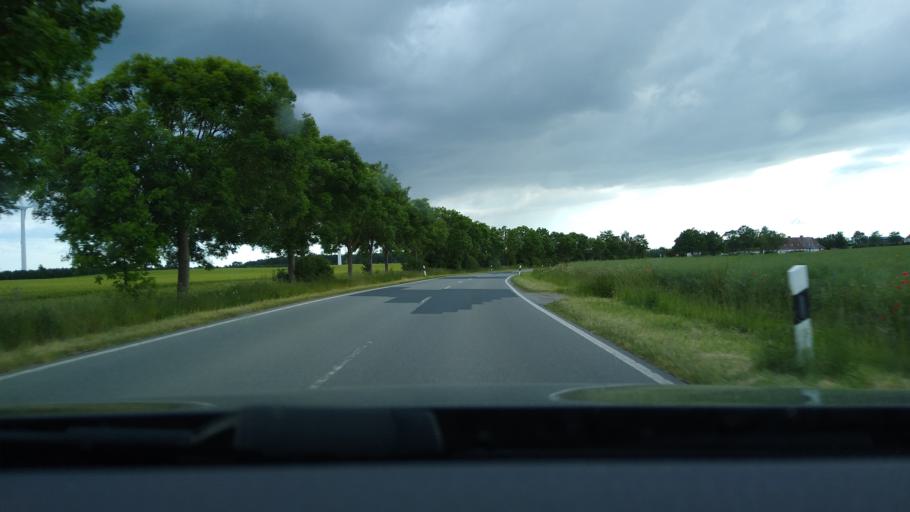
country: DE
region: Schleswig-Holstein
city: Kabelhorst
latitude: 54.2131
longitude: 10.9358
